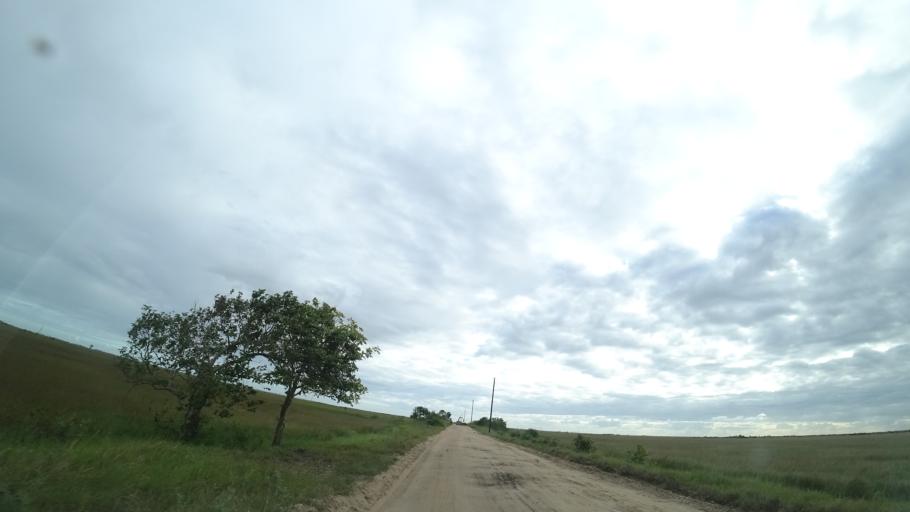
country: MZ
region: Sofala
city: Beira
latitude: -19.7414
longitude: 34.9618
